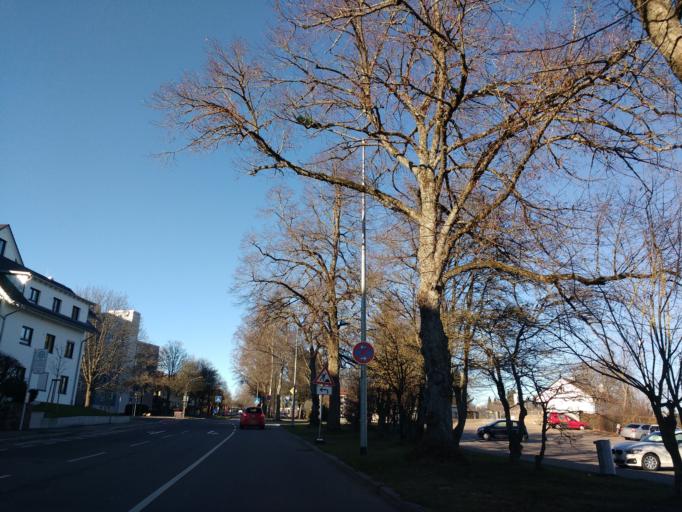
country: DE
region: Baden-Wuerttemberg
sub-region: Karlsruhe Region
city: Freudenstadt
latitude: 48.4699
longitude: 8.4138
